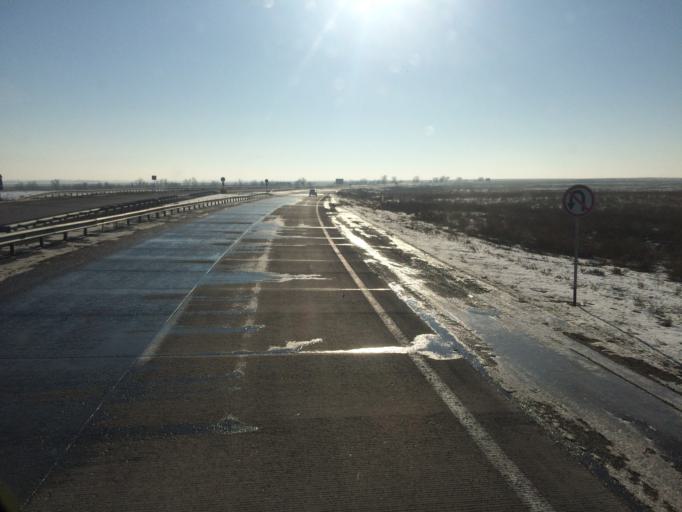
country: KG
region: Chuy
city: Kara-Balta
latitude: 43.1870
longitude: 73.9415
